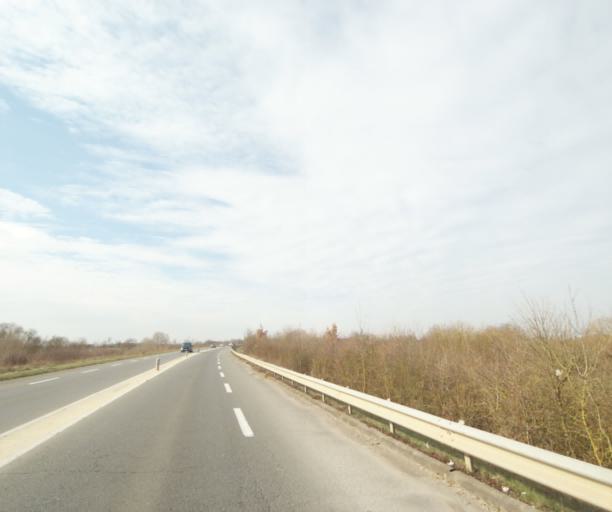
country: FR
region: Poitou-Charentes
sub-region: Departement des Deux-Sevres
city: Aiffres
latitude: 46.2967
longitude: -0.4441
